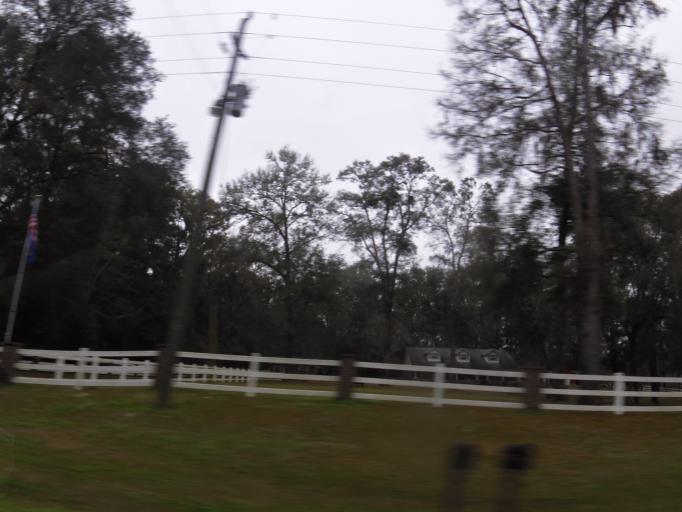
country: US
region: Florida
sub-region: Alachua County
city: High Springs
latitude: 29.8532
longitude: -82.5764
